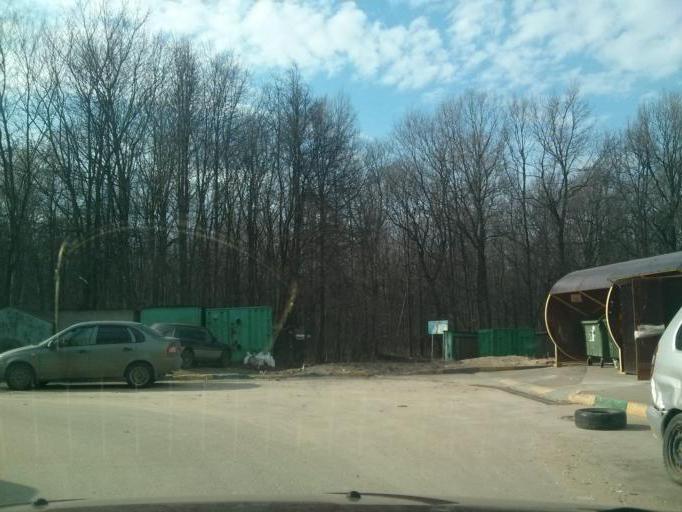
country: RU
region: Nizjnij Novgorod
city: Nizhniy Novgorod
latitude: 56.2662
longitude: 44.0152
